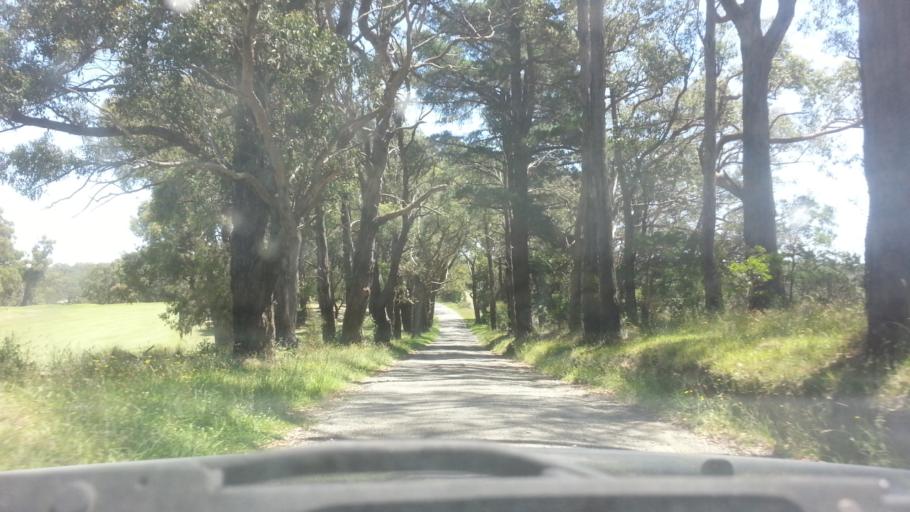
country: AU
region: Victoria
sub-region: Cardinia
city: Beaconsfield Upper
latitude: -37.9792
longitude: 145.4251
